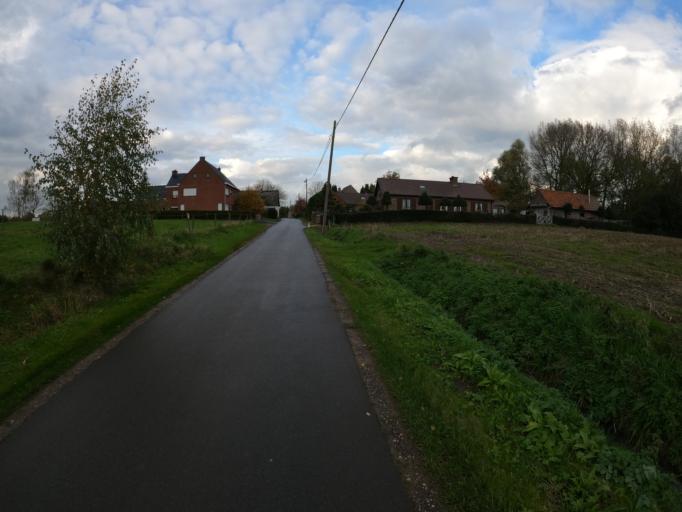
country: BE
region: Flanders
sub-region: Provincie Oost-Vlaanderen
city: Hamme
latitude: 51.1172
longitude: 4.1589
